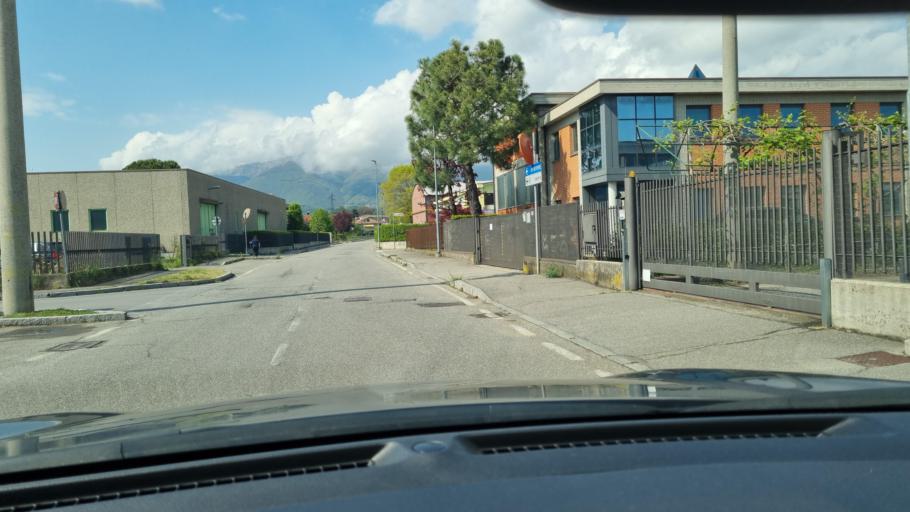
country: IT
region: Lombardy
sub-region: Provincia di Bergamo
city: Mapello
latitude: 45.7059
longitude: 9.5554
